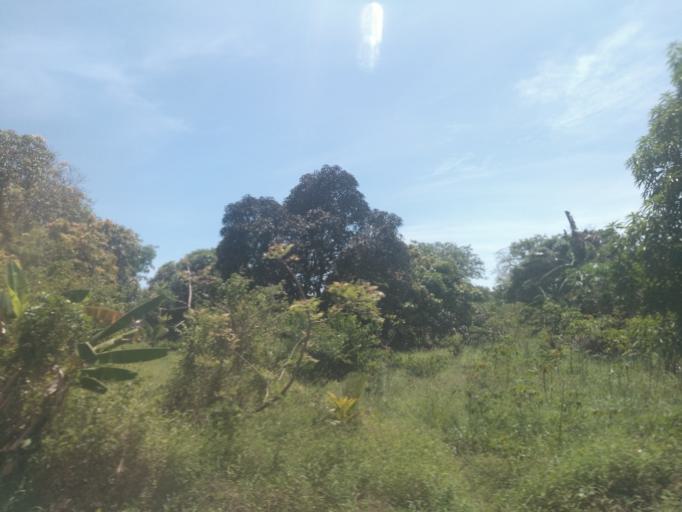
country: TZ
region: Zanzibar North
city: Gamba
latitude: -5.9304
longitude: 39.3416
